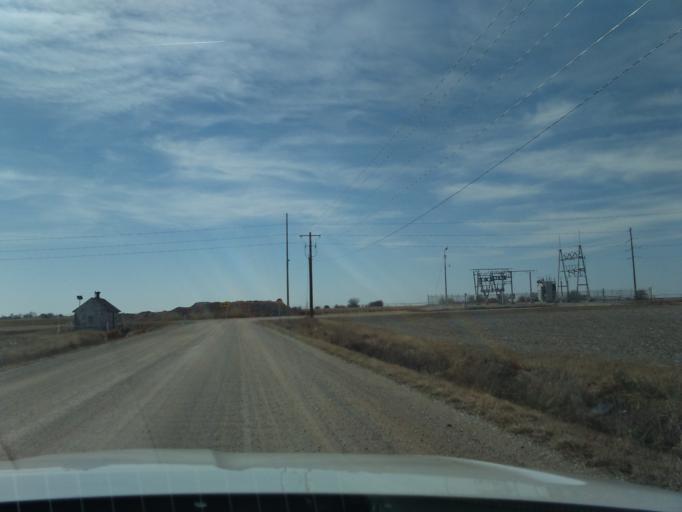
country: US
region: Nebraska
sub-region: Fillmore County
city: Geneva
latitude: 40.6266
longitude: -97.5852
